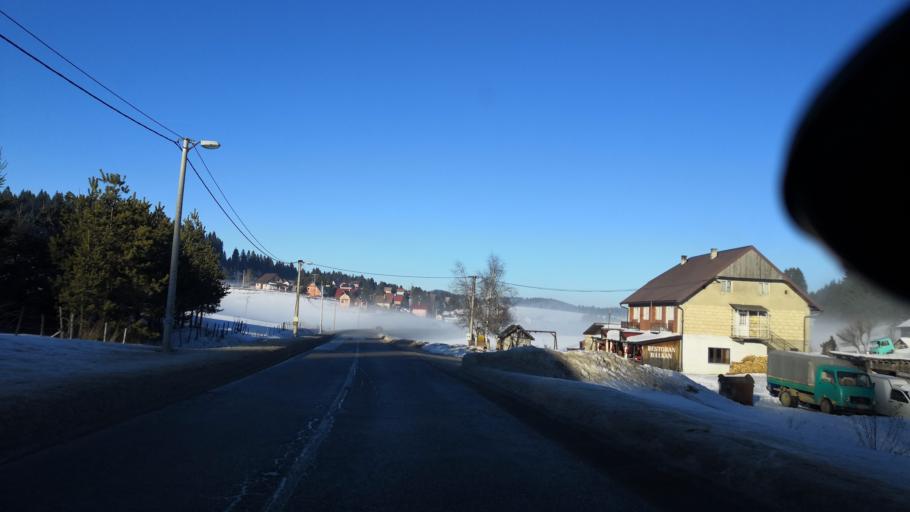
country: BA
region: Republika Srpska
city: Han Pijesak
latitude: 44.0910
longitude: 18.9547
